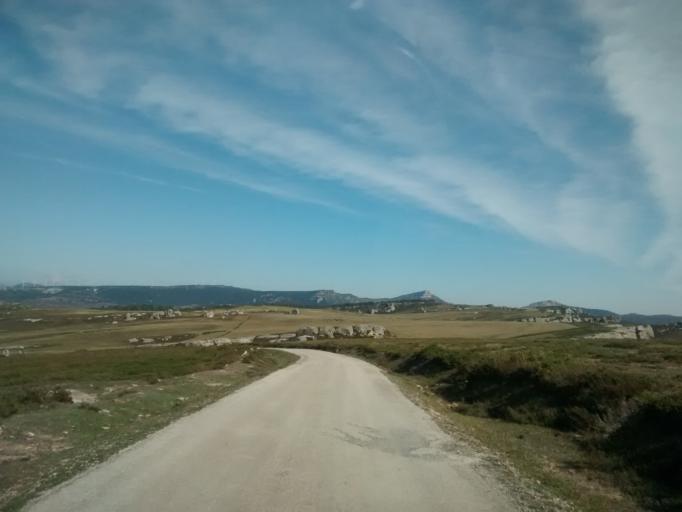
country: ES
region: Castille and Leon
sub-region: Provincia de Burgos
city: Arija
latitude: 42.9347
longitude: -3.9524
